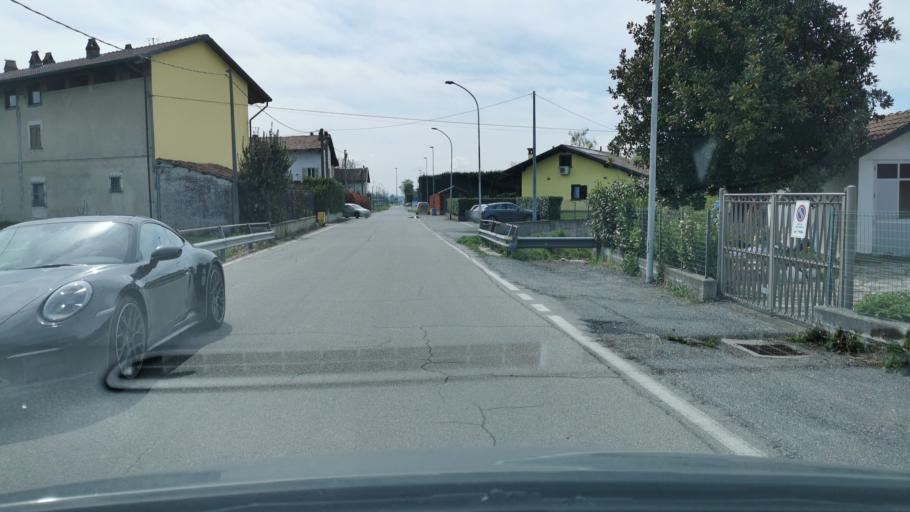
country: IT
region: Piedmont
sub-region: Provincia di Torino
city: Busano
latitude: 45.3284
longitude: 7.6571
